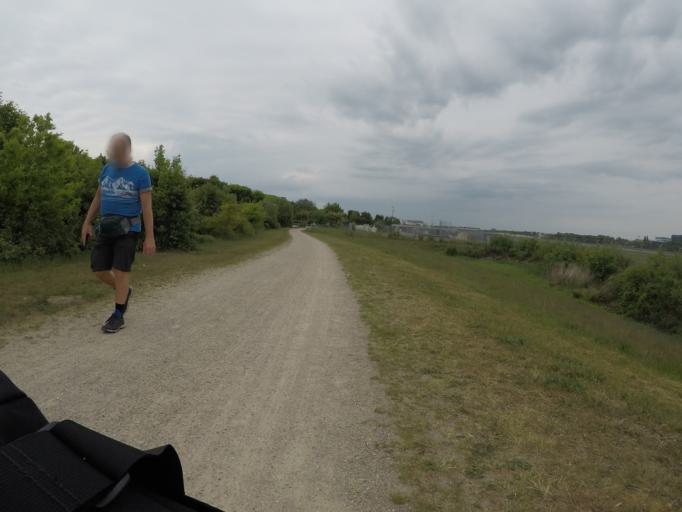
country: DE
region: Hamburg
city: Langenhorn
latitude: 53.6454
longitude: 9.9796
